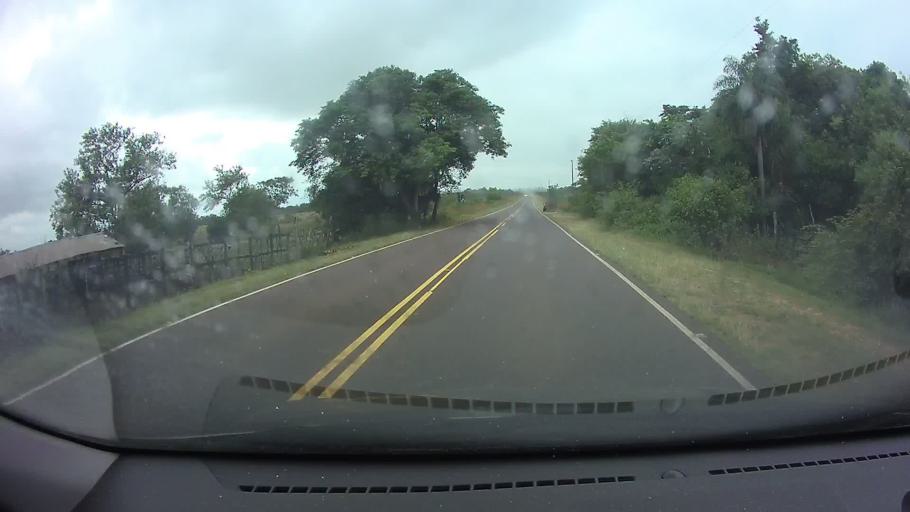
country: PY
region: Central
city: Nueva Italia
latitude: -25.6195
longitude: -57.4005
